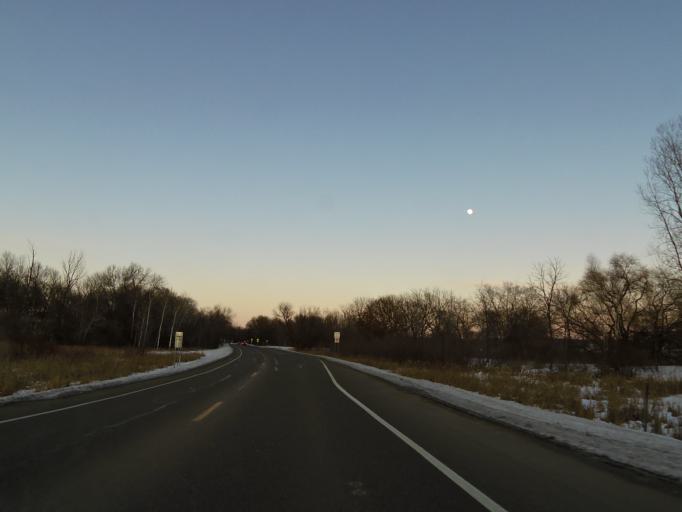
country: US
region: Minnesota
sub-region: Ramsey County
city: White Bear Lake
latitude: 45.0942
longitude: -93.0001
